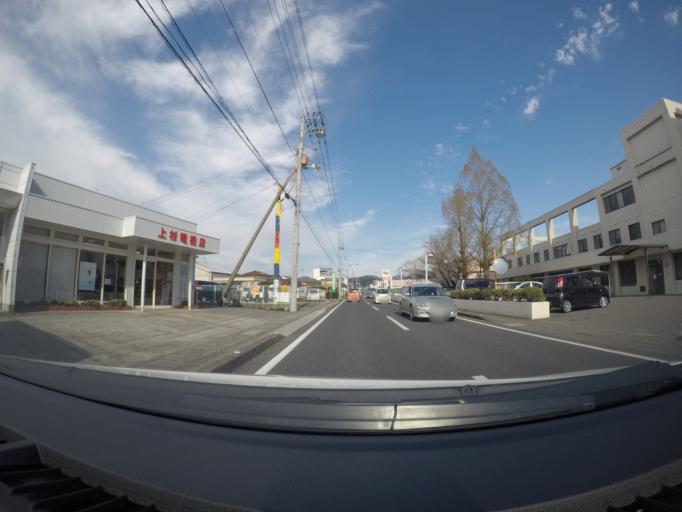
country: JP
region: Kochi
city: Kochi-shi
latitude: 33.6082
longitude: 133.6970
